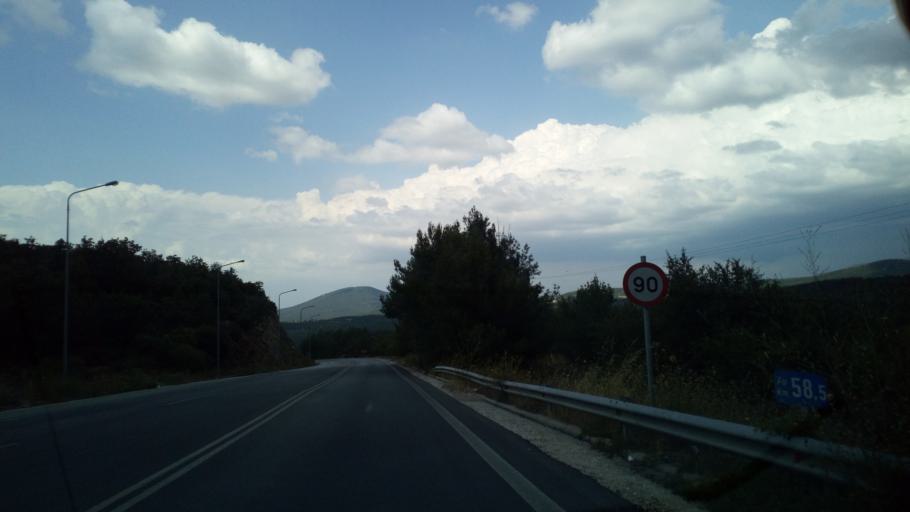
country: GR
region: Central Macedonia
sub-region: Nomos Chalkidikis
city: Polygyros
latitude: 40.4083
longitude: 23.4216
